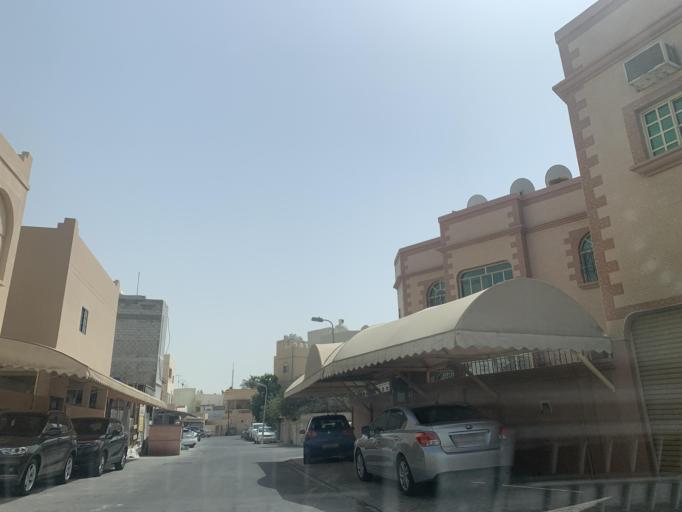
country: BH
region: Northern
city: Madinat `Isa
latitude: 26.1773
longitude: 50.5575
